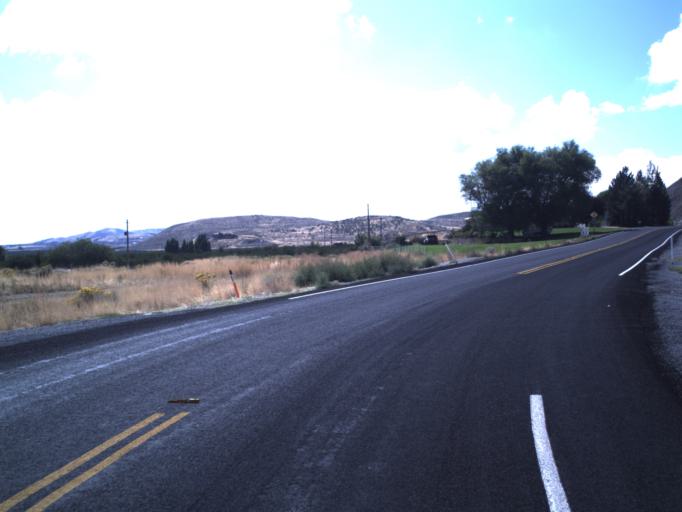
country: US
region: Utah
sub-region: Utah County
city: Santaquin
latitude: 40.0170
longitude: -111.7949
